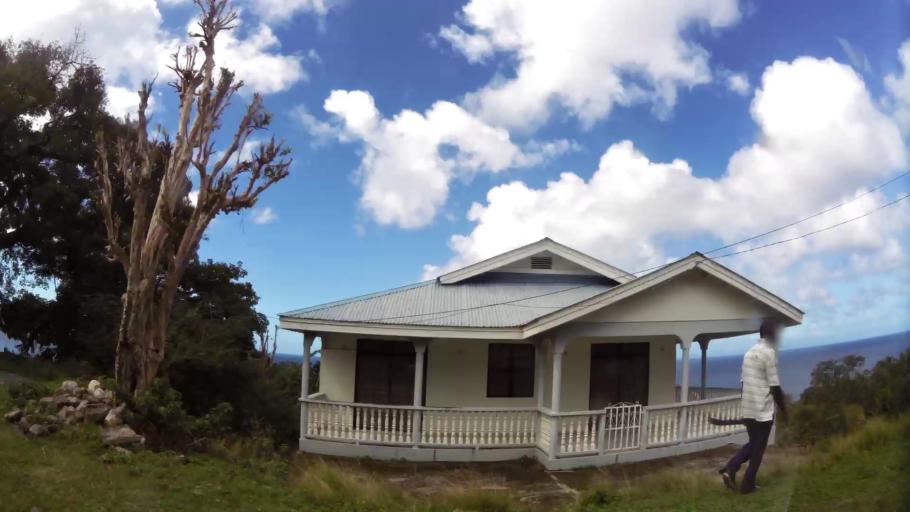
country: DM
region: Saint John
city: Portsmouth
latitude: 15.6306
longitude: -61.4623
